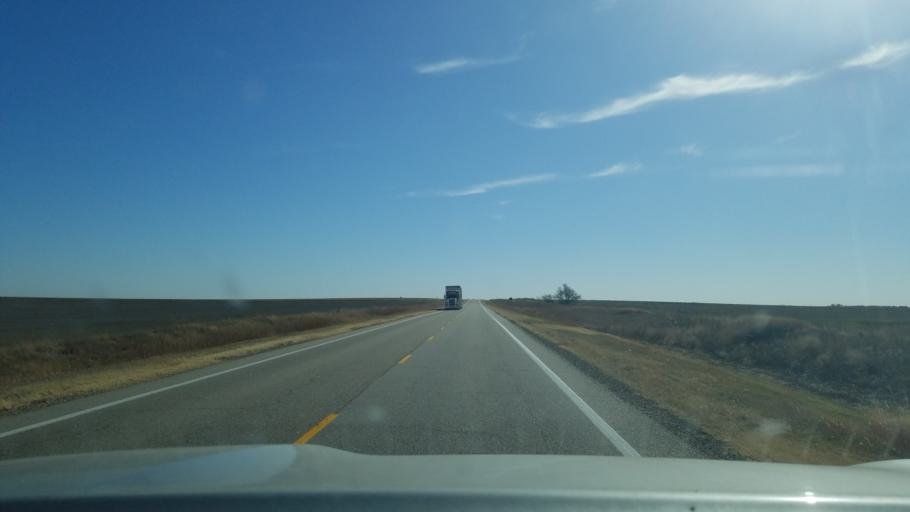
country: US
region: Kansas
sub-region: Ford County
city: Dodge City
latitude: 37.5828
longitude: -99.6785
